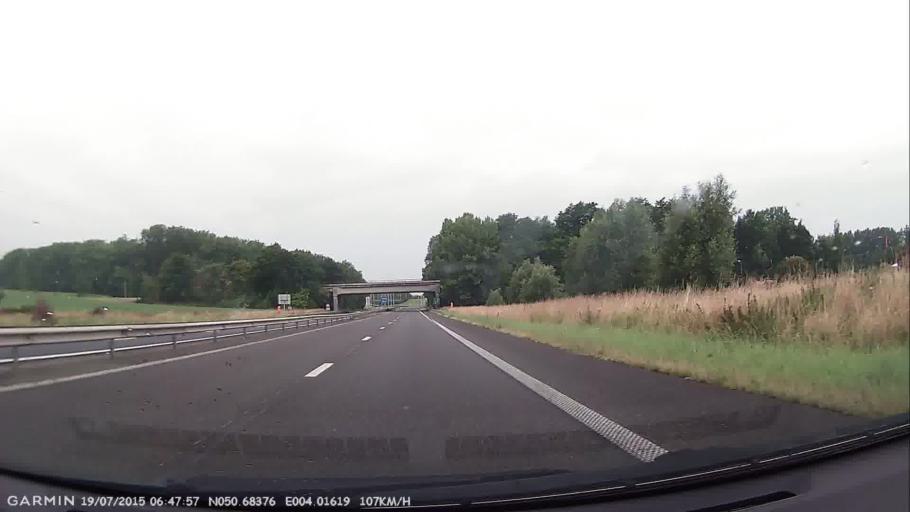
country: BE
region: Wallonia
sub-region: Province du Hainaut
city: Enghien
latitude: 50.6838
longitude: 4.0162
